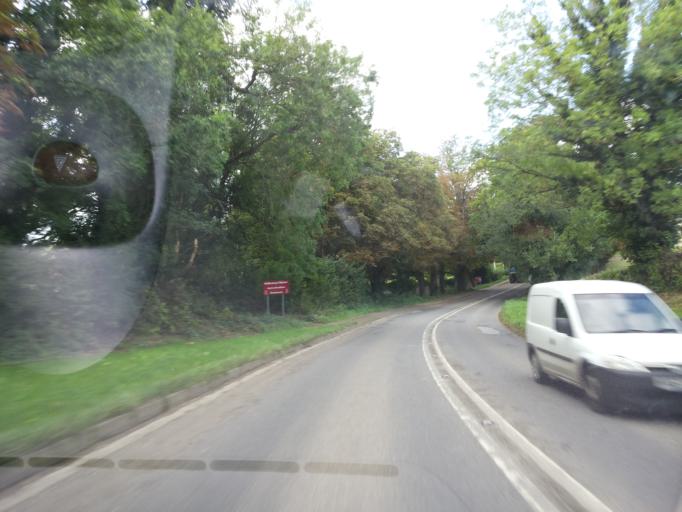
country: GB
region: England
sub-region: Wiltshire
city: Shrewton
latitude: 51.1877
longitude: -1.8952
